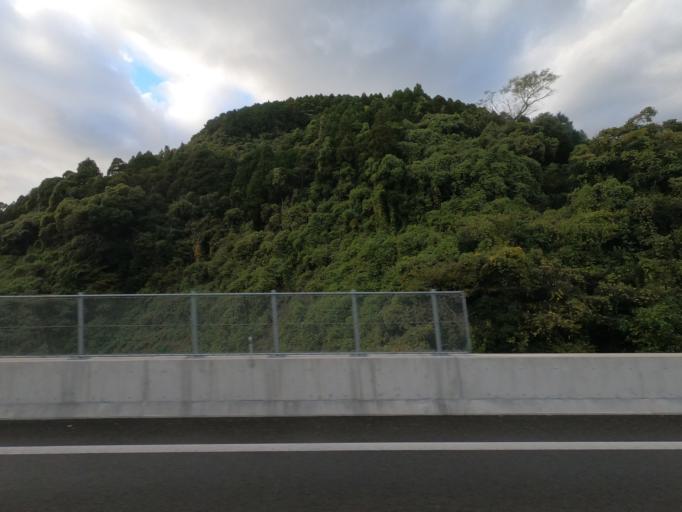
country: JP
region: Kumamoto
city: Minamata
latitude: 32.2236
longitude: 130.4319
